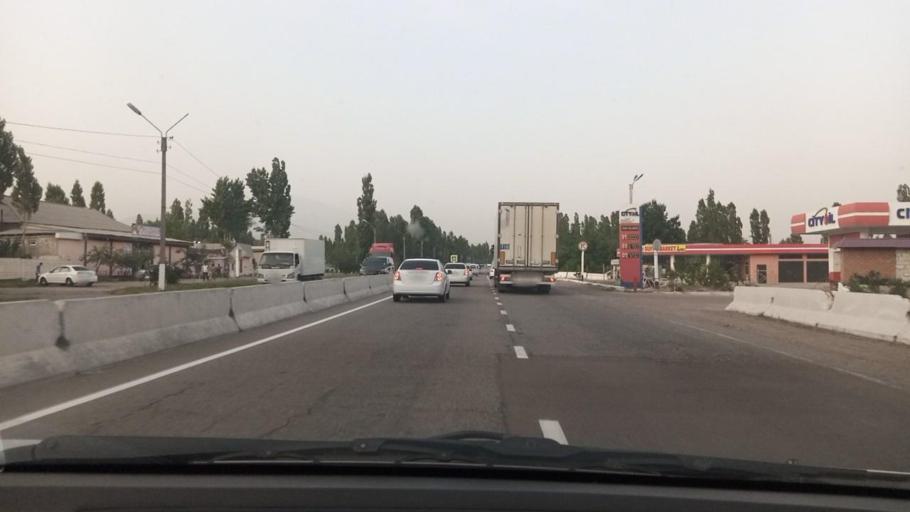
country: UZ
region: Toshkent
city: Angren
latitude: 40.9903
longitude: 70.0412
